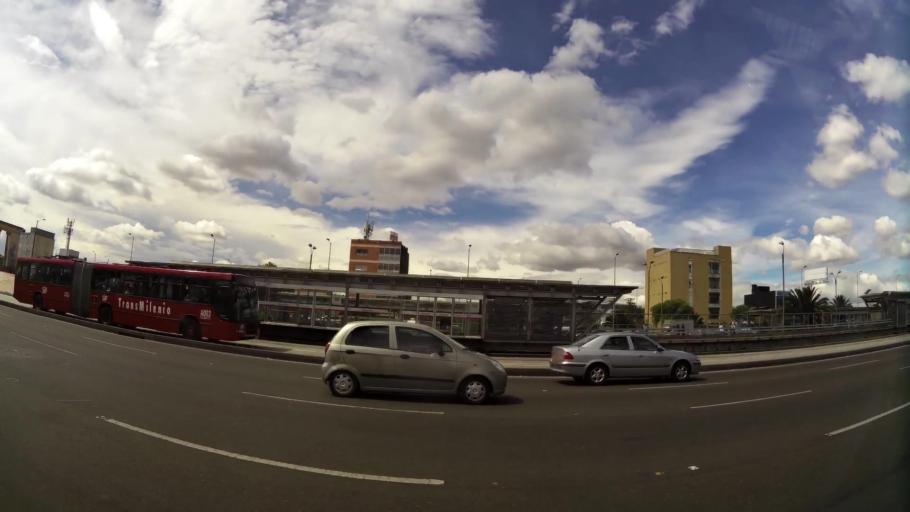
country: CO
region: Bogota D.C.
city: Bogota
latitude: 4.6295
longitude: -74.1308
